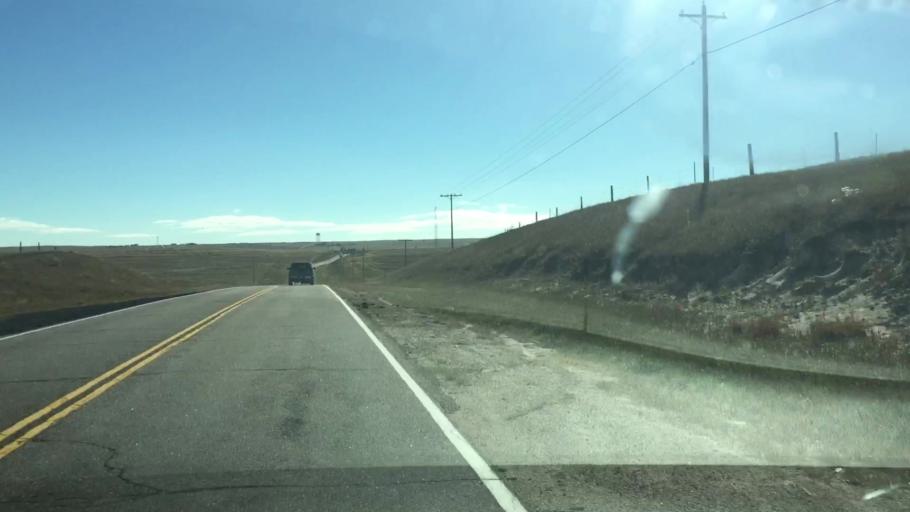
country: US
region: Colorado
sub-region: Elbert County
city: Kiowa
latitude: 39.3509
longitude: -104.4900
